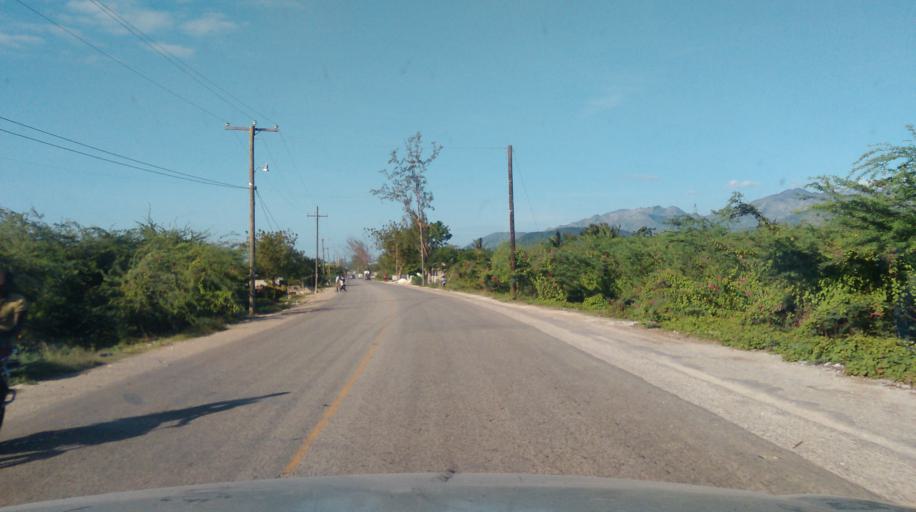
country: HT
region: Sud
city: Aquin
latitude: 18.3076
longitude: -73.3233
